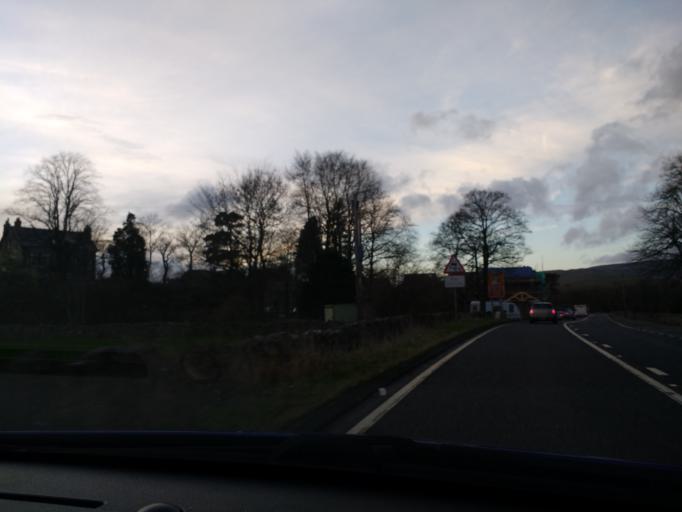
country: GB
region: England
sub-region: North Yorkshire
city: Ingleton
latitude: 54.1427
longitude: -2.4634
